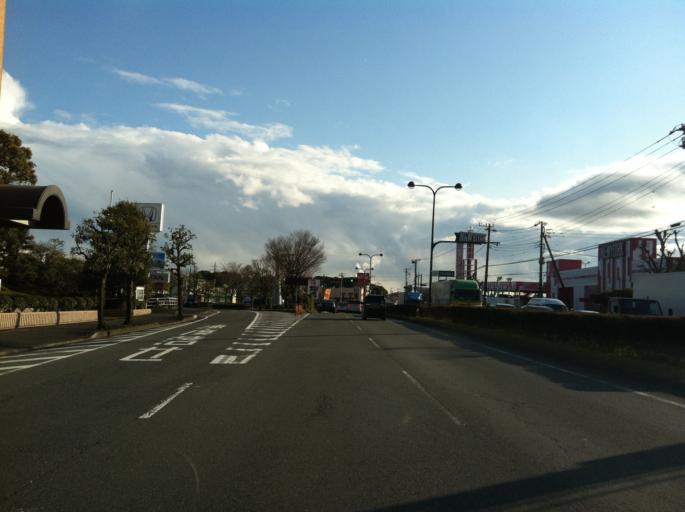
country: JP
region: Shizuoka
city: Fuji
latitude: 35.1656
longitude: 138.6701
